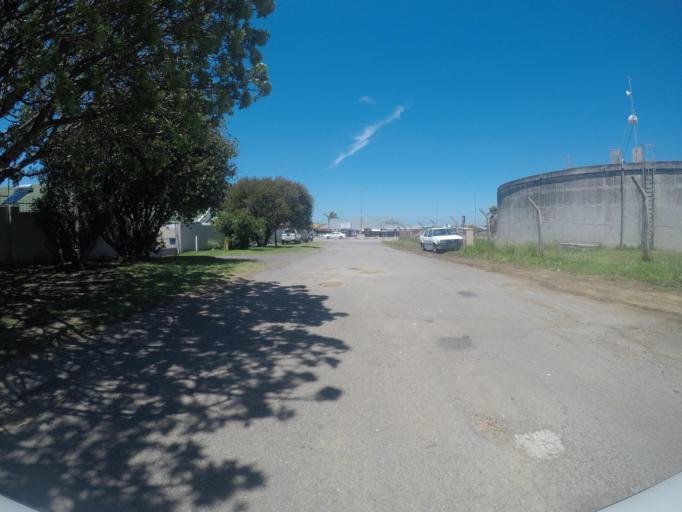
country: ZA
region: Eastern Cape
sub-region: Buffalo City Metropolitan Municipality
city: East London
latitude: -32.9343
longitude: 27.9958
